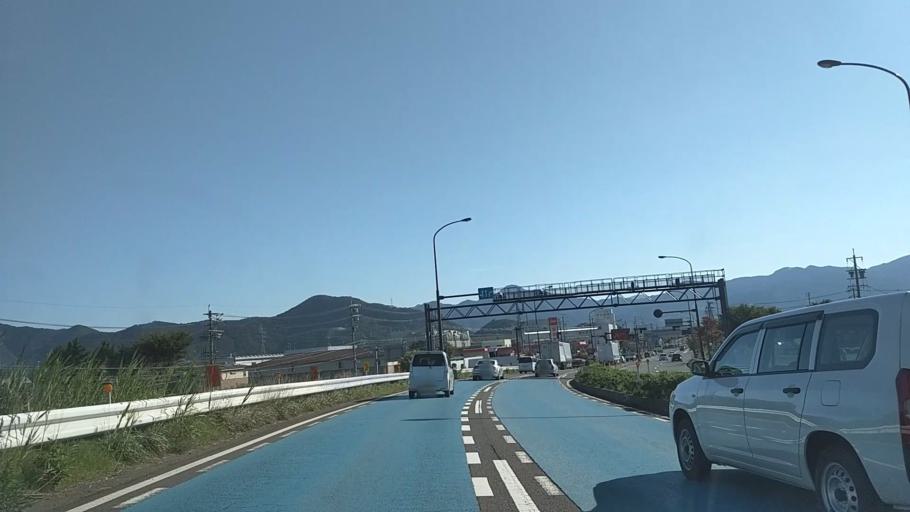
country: JP
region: Nagano
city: Nagano-shi
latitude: 36.5558
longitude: 138.1385
